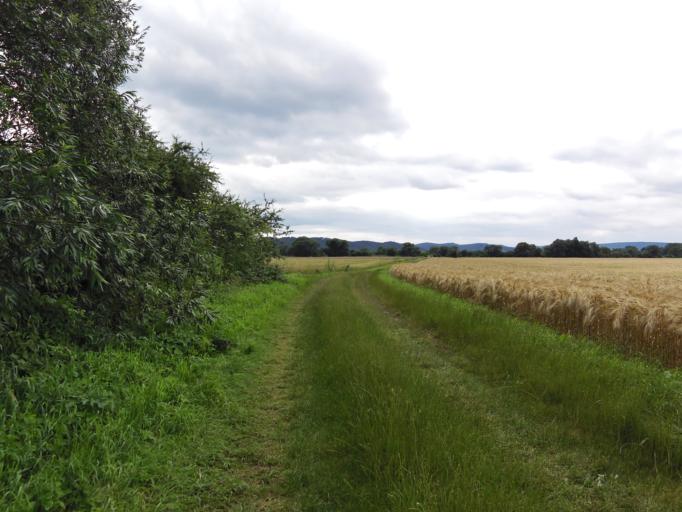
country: DE
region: Hesse
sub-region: Regierungsbezirk Kassel
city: Herleshausen
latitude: 50.9985
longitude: 10.1809
